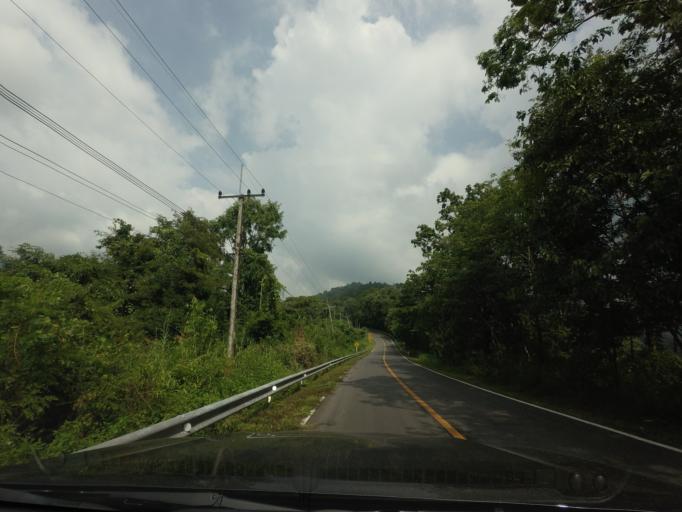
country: TH
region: Nan
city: Pua
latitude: 19.1848
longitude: 101.0083
